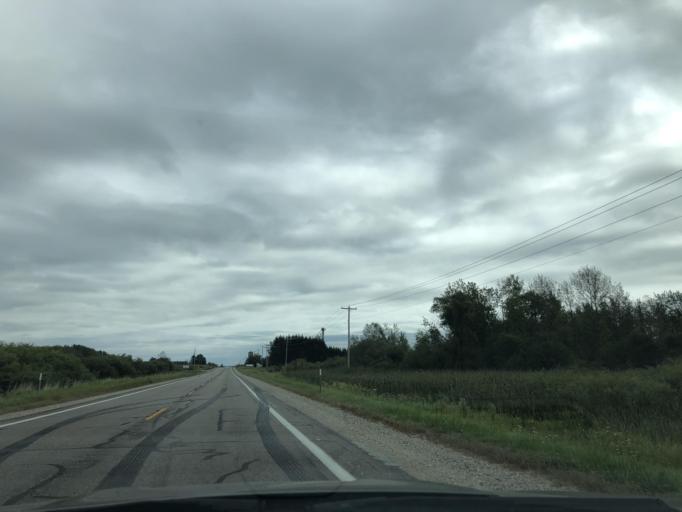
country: US
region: Michigan
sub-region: Missaukee County
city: Lake City
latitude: 44.1937
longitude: -85.1924
